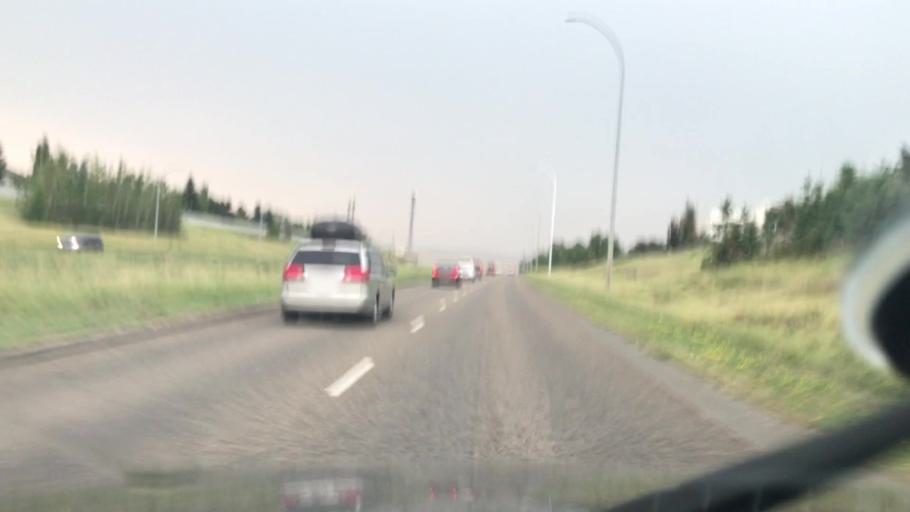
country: CA
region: Alberta
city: Edmonton
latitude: 53.4653
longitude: -113.5845
